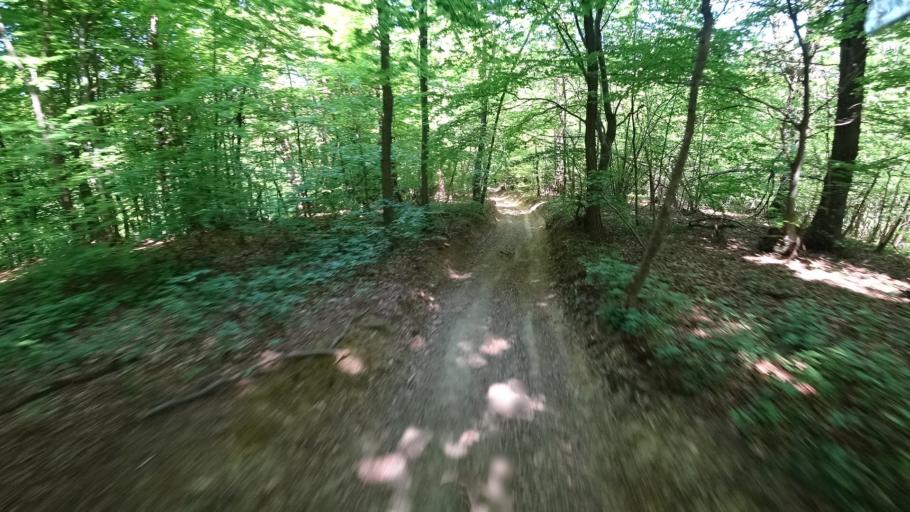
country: HR
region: Zagrebacka
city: Jablanovec
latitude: 45.8490
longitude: 15.8532
